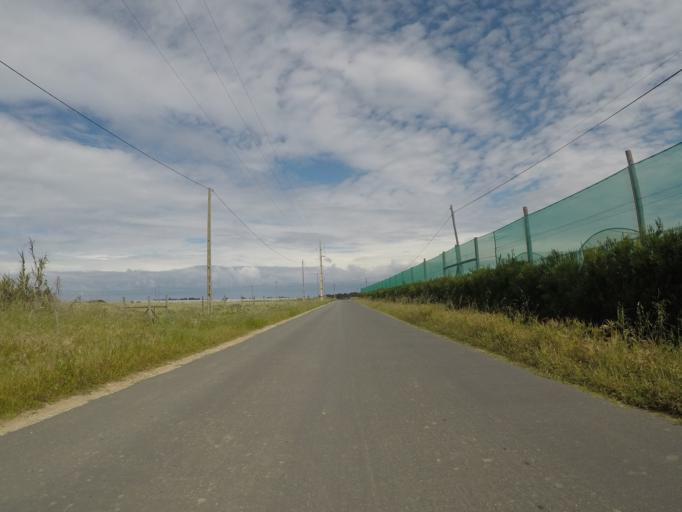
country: PT
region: Beja
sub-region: Odemira
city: Sao Teotonio
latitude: 37.4858
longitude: -8.7724
